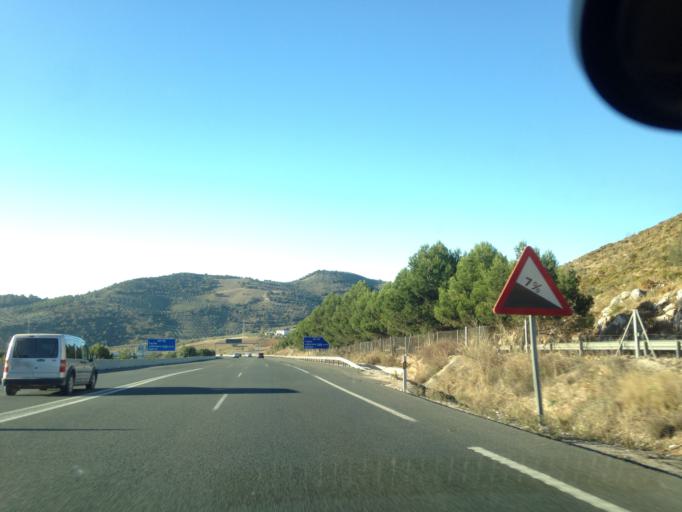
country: ES
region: Andalusia
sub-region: Provincia de Malaga
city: Casabermeja
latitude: 36.9648
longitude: -4.4444
